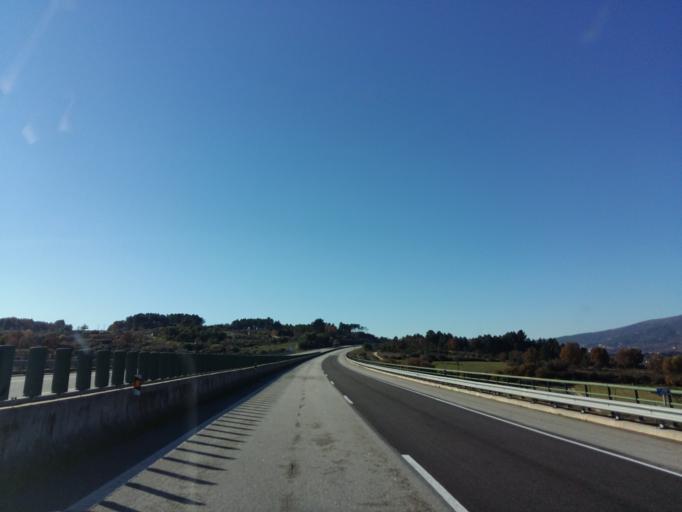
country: PT
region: Castelo Branco
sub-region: Covilha
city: Covilha
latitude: 40.2478
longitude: -7.4578
